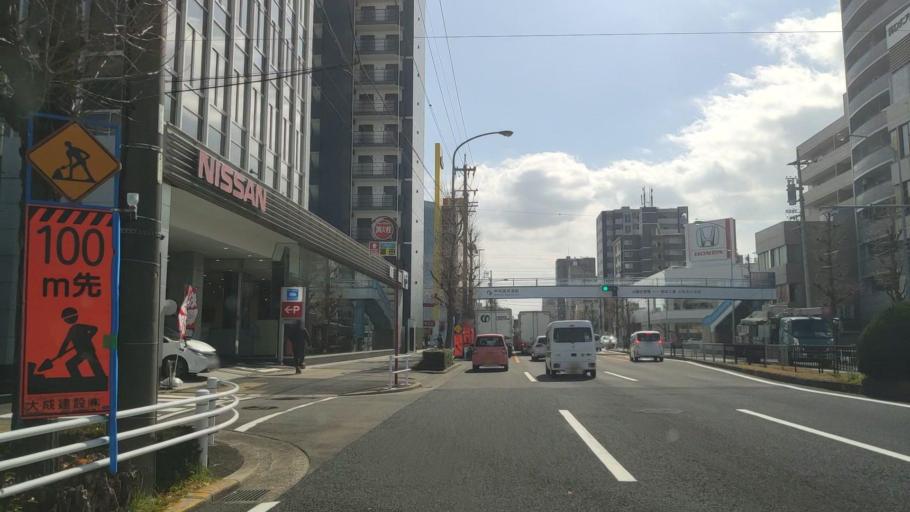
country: JP
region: Aichi
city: Nagoya-shi
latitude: 35.1785
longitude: 136.8730
